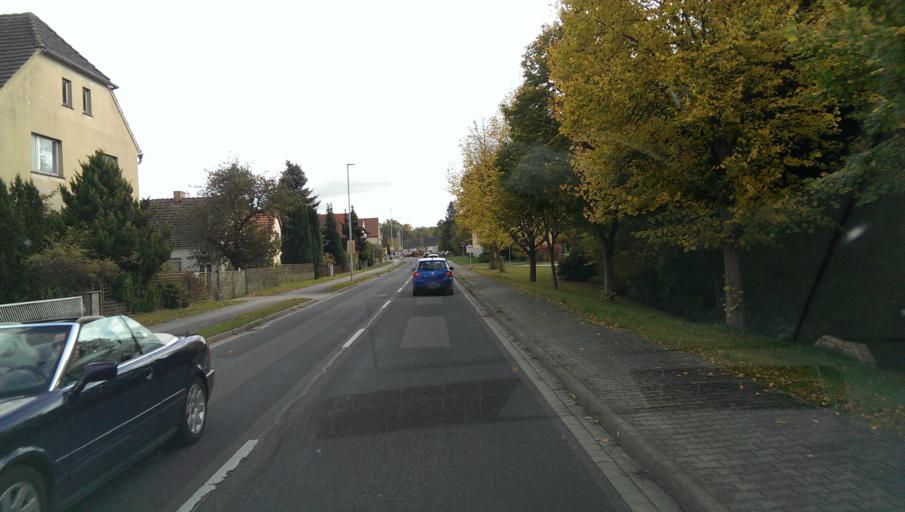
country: DE
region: Brandenburg
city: Guteborn
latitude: 51.4224
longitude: 13.9233
